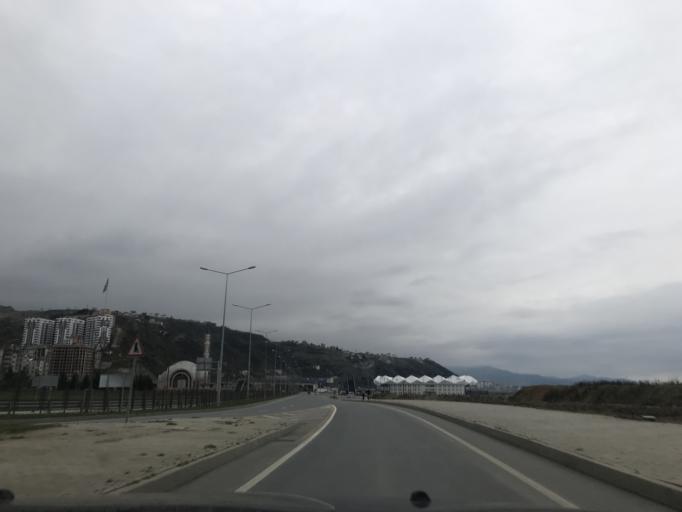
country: TR
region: Trabzon
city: Trabzon
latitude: 40.9958
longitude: 39.6627
